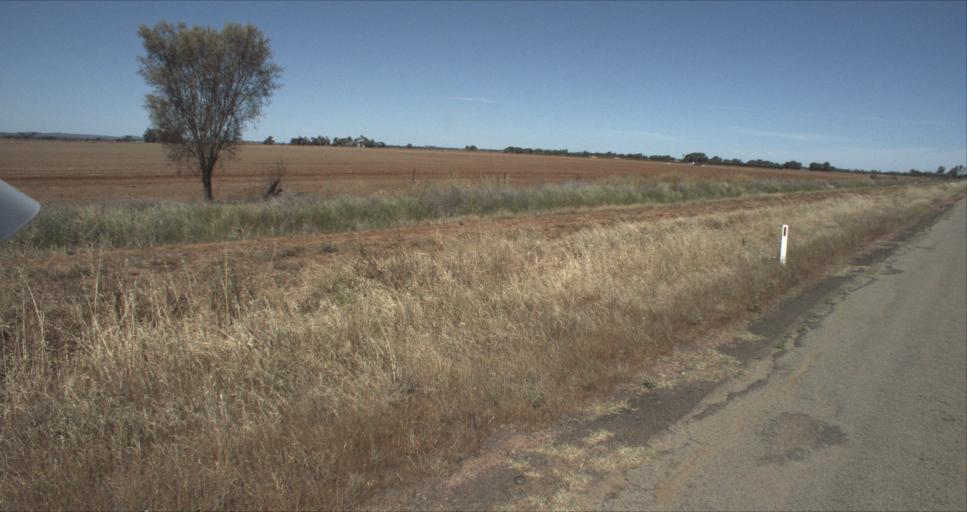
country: AU
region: New South Wales
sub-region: Leeton
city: Leeton
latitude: -34.5168
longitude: 146.3453
